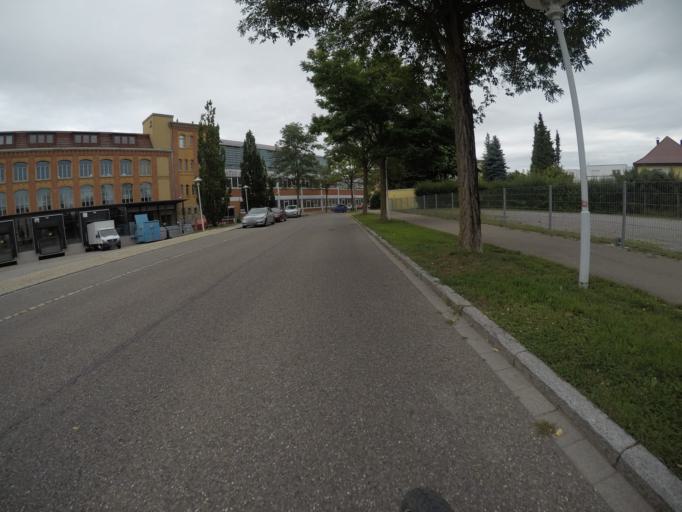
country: DE
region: Baden-Wuerttemberg
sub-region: Regierungsbezirk Stuttgart
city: Herrenberg
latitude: 48.5925
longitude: 8.8626
